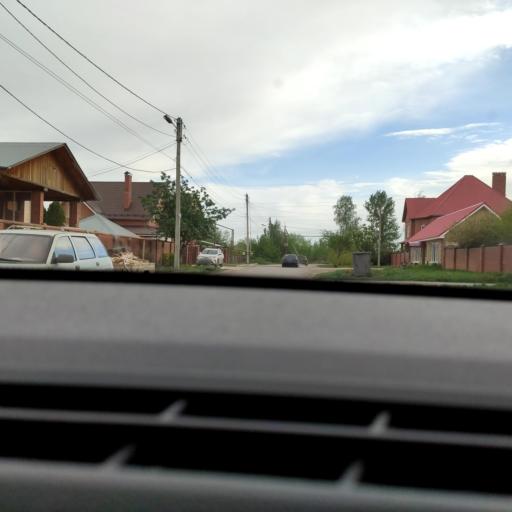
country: RU
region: Samara
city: Tol'yatti
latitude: 53.5617
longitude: 49.3807
